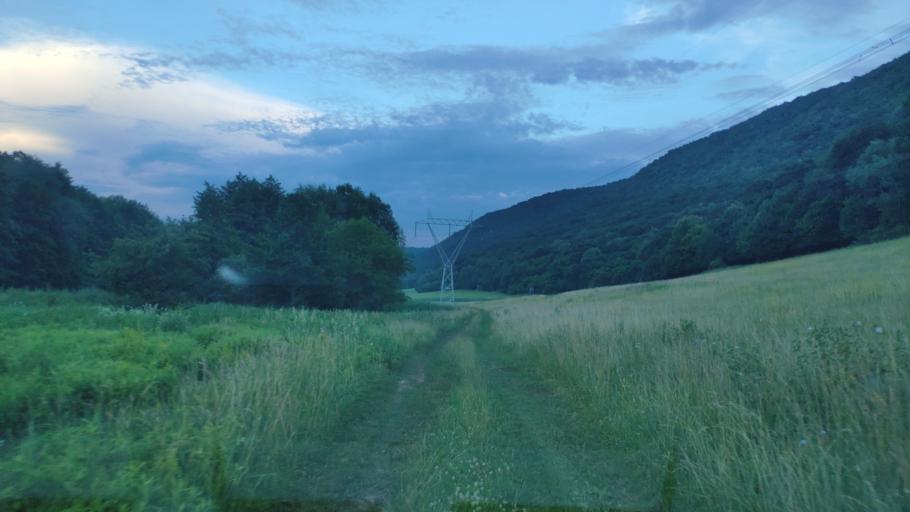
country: SK
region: Kosicky
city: Medzev
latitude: 48.5849
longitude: 20.7557
